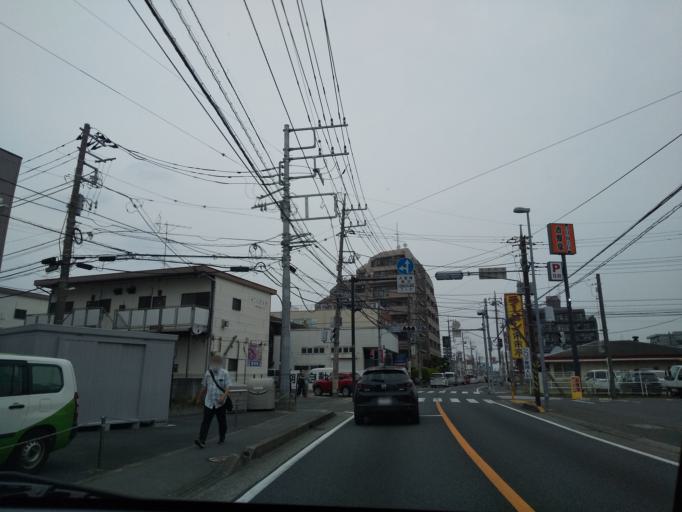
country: JP
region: Kanagawa
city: Zama
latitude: 35.5037
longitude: 139.4104
